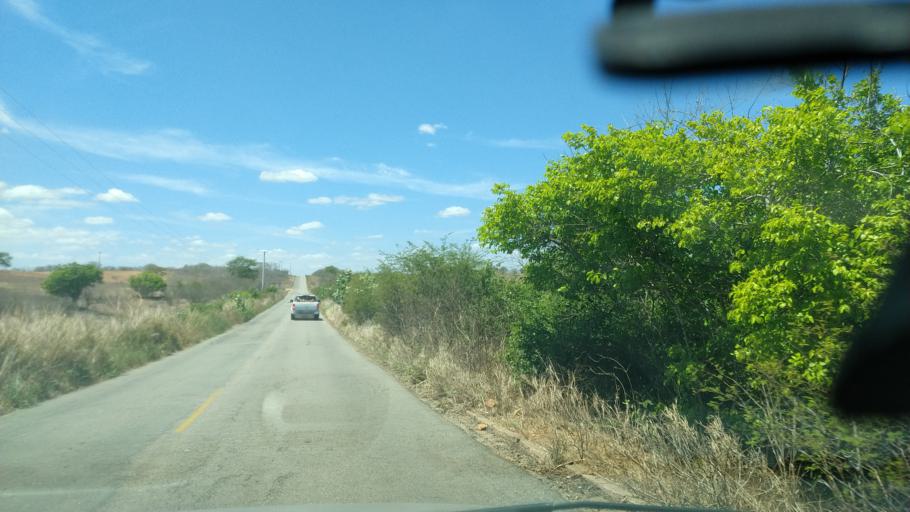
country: BR
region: Rio Grande do Norte
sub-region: Sao Paulo Do Potengi
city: Sao Paulo do Potengi
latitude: -5.9033
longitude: -35.6128
